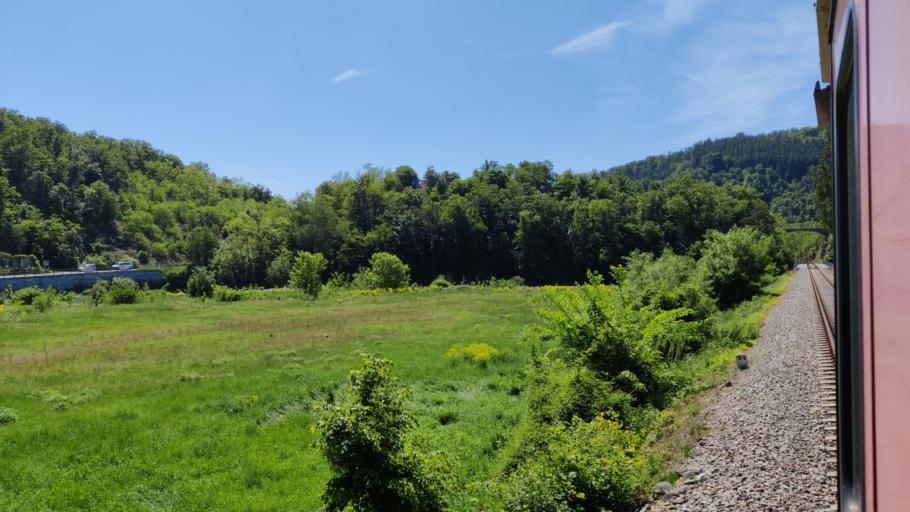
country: AT
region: Lower Austria
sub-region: Politischer Bezirk Horn
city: Gars am Kamp
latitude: 48.5756
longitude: 15.6588
